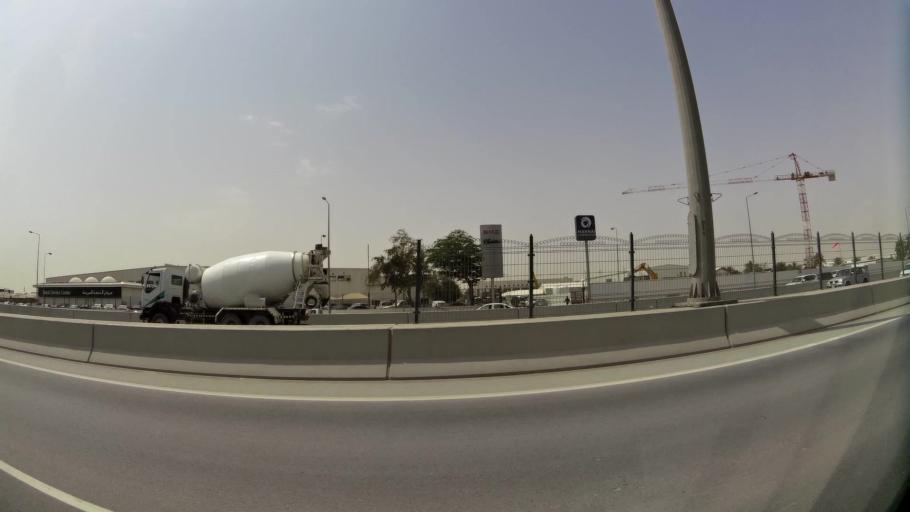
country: QA
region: Baladiyat ar Rayyan
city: Ar Rayyan
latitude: 25.2171
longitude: 51.4380
